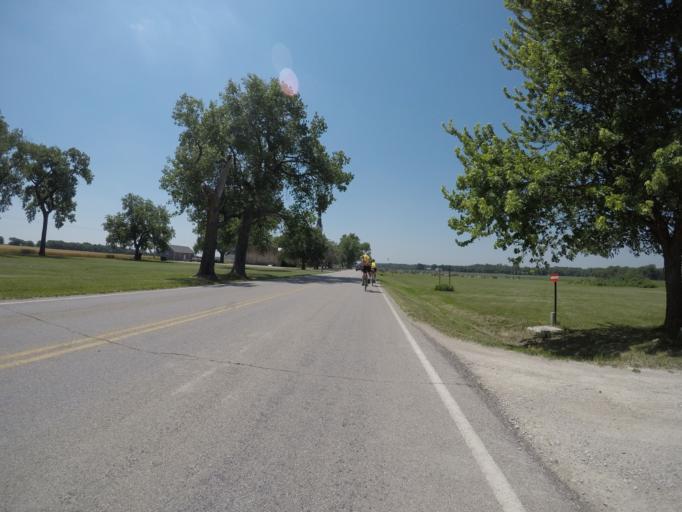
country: US
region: Kansas
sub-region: Pottawatomie County
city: Westmoreland
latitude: 39.2963
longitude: -96.4407
